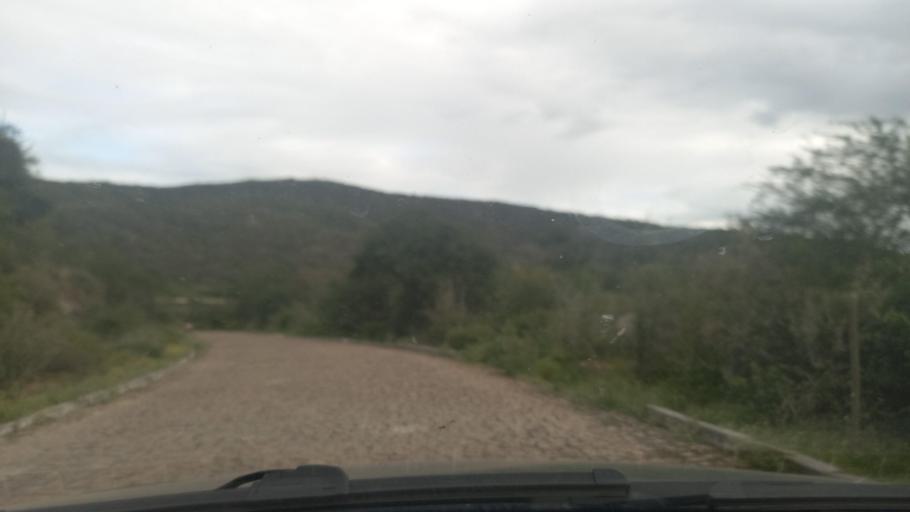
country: BR
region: Sergipe
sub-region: Caninde De Sao Francisco
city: Caninde de Sao Francisco
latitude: -9.6254
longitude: -37.8074
